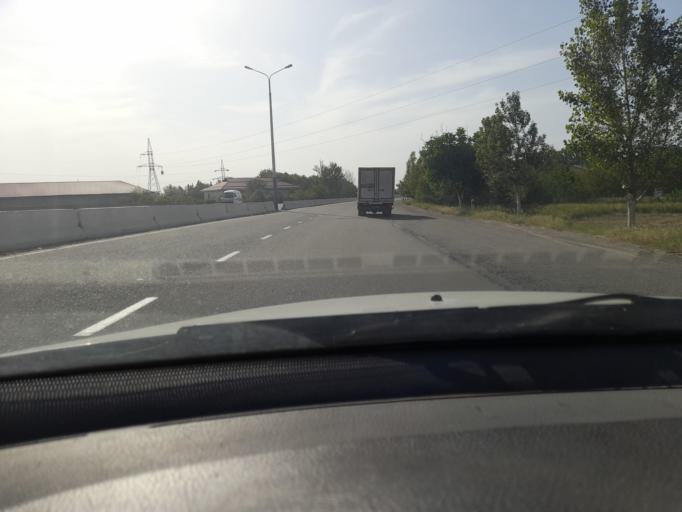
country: UZ
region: Samarqand
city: Kattaqo'rg'on
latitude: 39.9238
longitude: 66.2773
